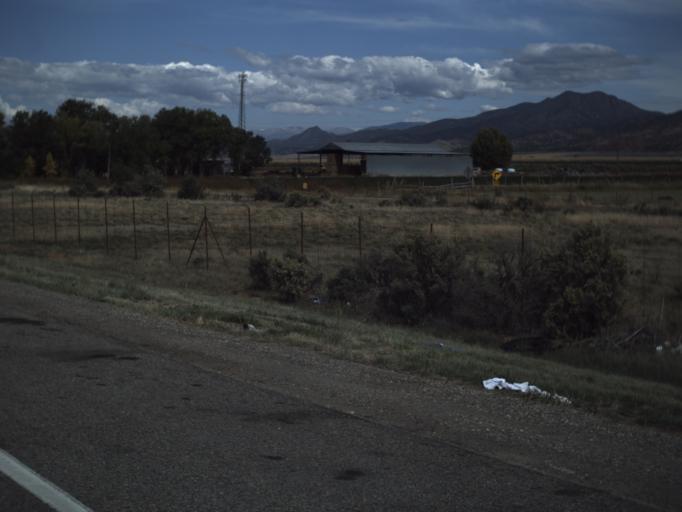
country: US
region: Utah
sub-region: Iron County
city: Parowan
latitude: 37.9088
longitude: -112.7758
